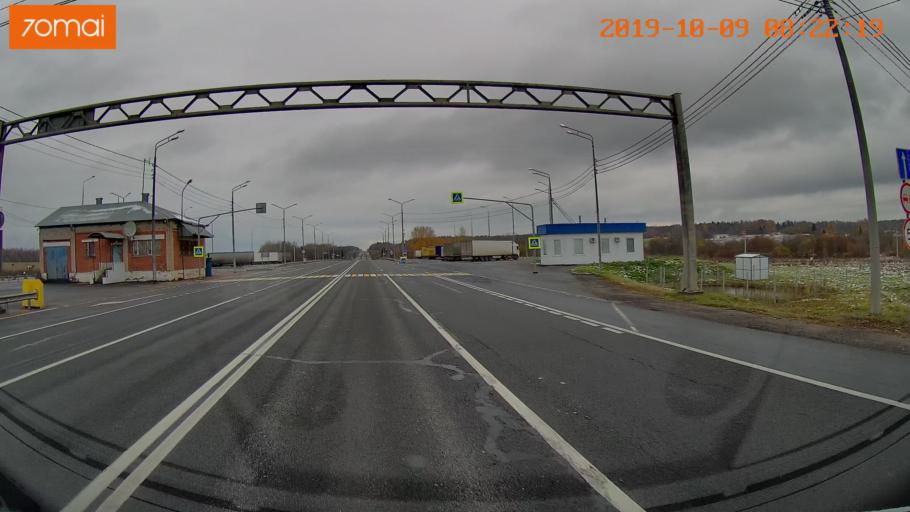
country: RU
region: Vologda
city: Gryazovets
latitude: 58.7421
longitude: 40.2891
